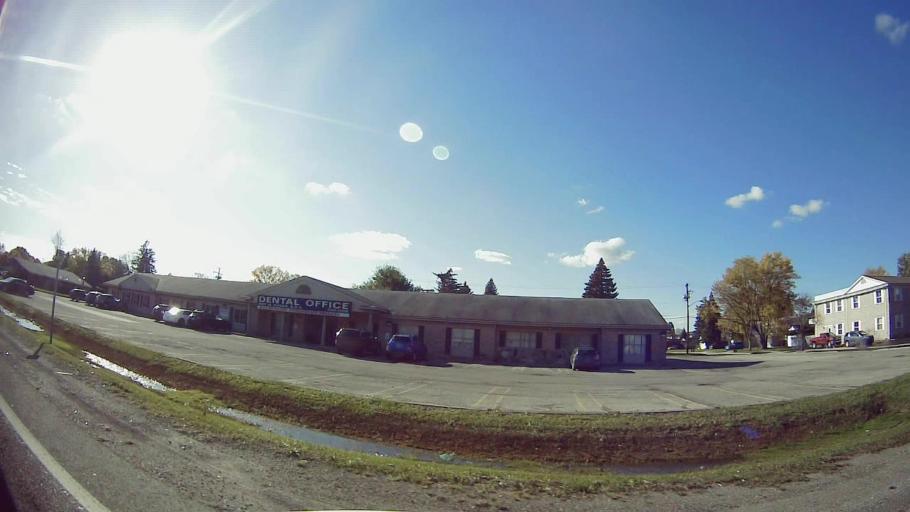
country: US
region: Michigan
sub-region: Oakland County
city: Southfield
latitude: 42.4777
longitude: -83.2215
